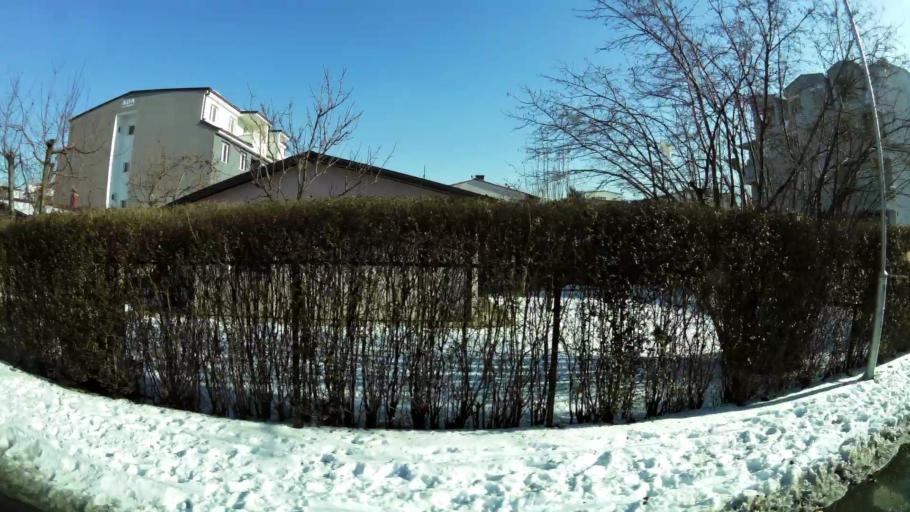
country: MK
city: Krushopek
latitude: 42.0036
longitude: 21.3745
